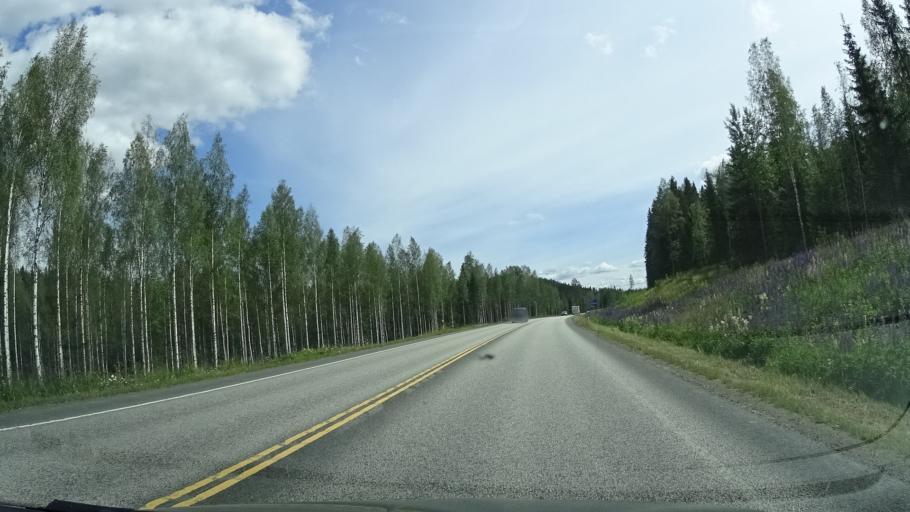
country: FI
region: Central Finland
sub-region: Jyvaeskylae
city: Jyvaeskylae
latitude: 62.2530
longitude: 25.6368
